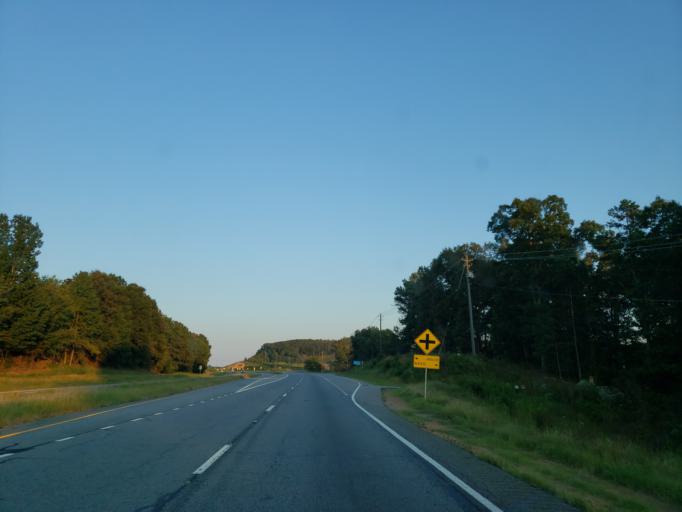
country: US
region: Georgia
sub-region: Bartow County
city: Euharlee
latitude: 34.2206
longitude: -84.8799
